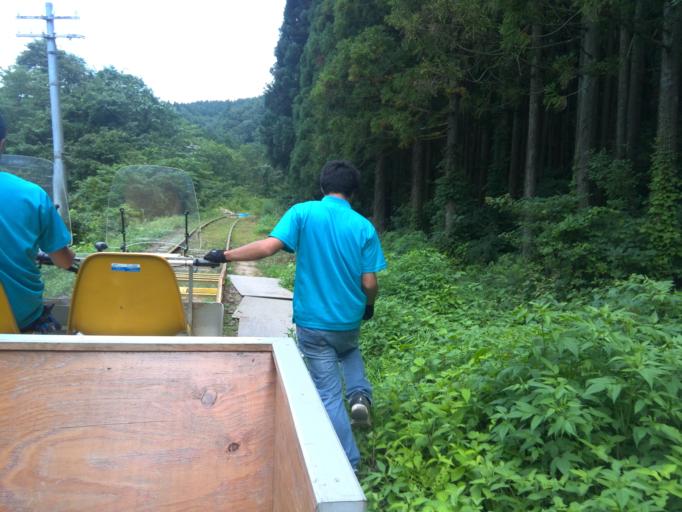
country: JP
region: Akita
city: Odate
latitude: 40.2974
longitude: 140.6474
